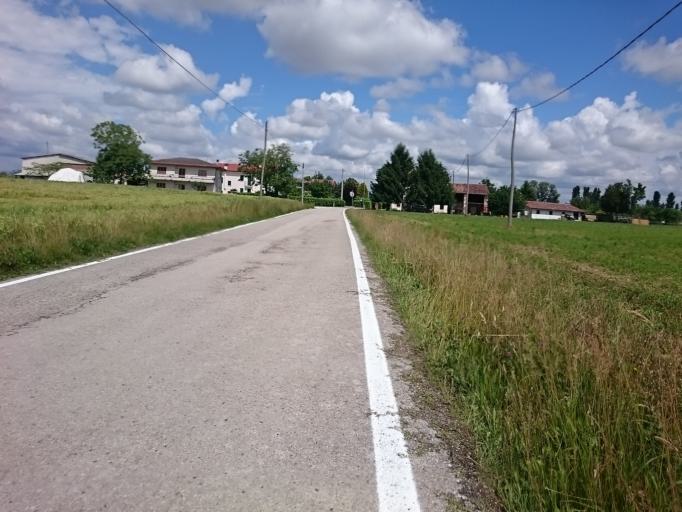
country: IT
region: Veneto
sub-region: Provincia di Padova
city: Campodoro
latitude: 45.4814
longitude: 11.7373
